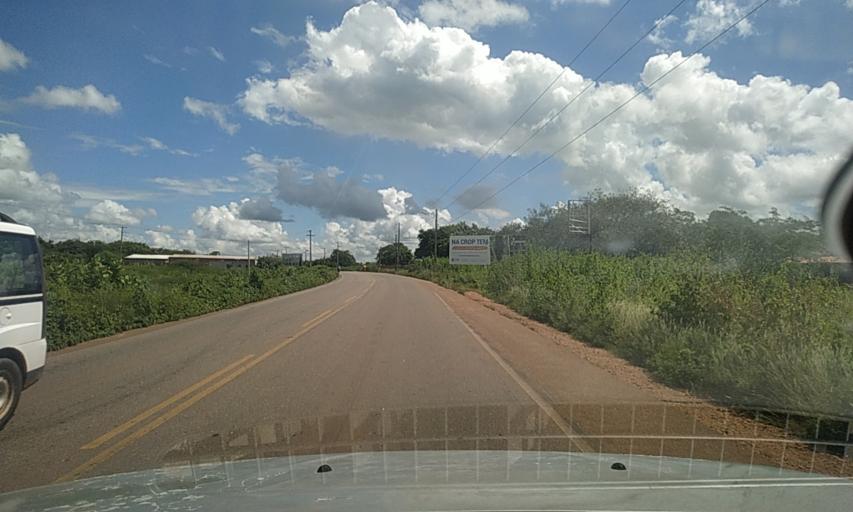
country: BR
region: Rio Grande do Norte
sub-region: Mossoro
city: Mossoro
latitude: -5.1854
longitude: -37.3855
